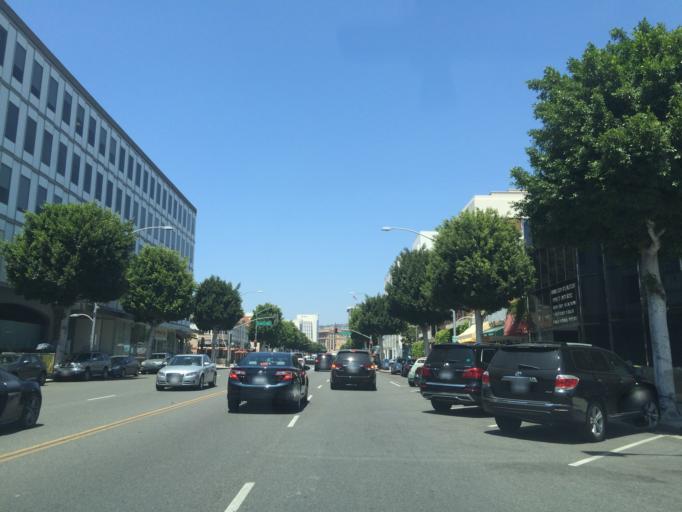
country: US
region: California
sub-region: Los Angeles County
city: Beverly Hills
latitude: 34.0613
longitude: -118.3990
